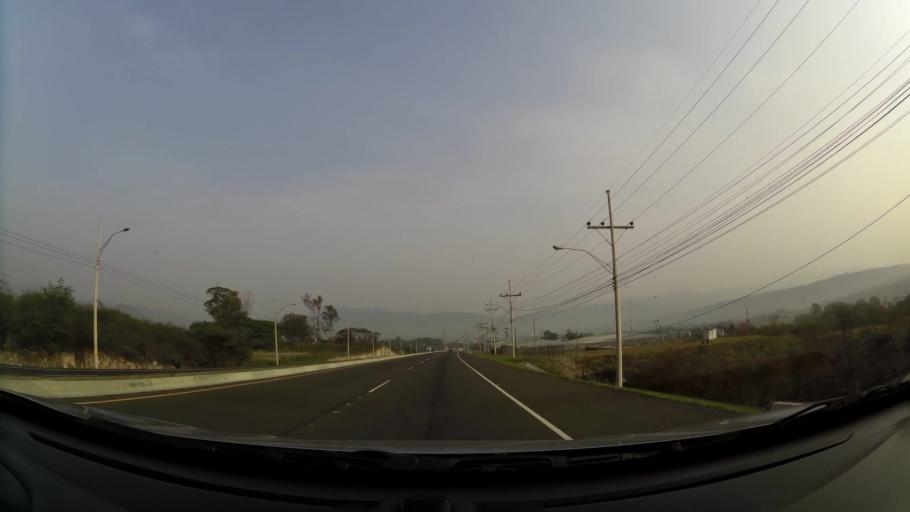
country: HN
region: Francisco Morazan
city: Tamara
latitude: 14.2057
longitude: -87.3493
